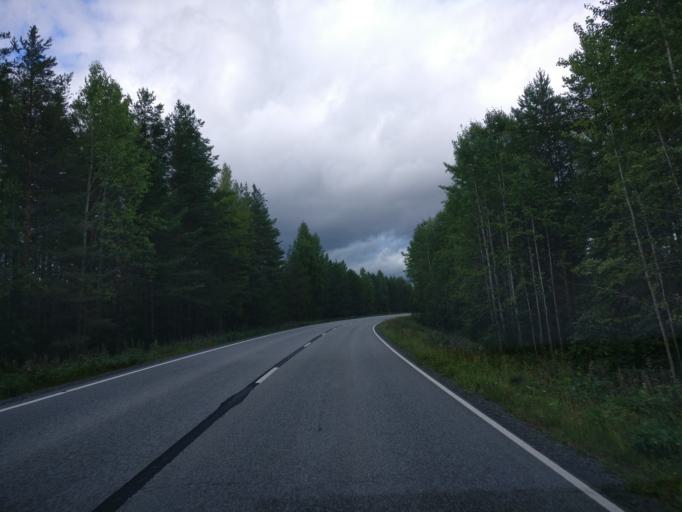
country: FI
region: Central Finland
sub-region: Jyvaeskylae
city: Toivakka
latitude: 62.1287
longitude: 26.1028
